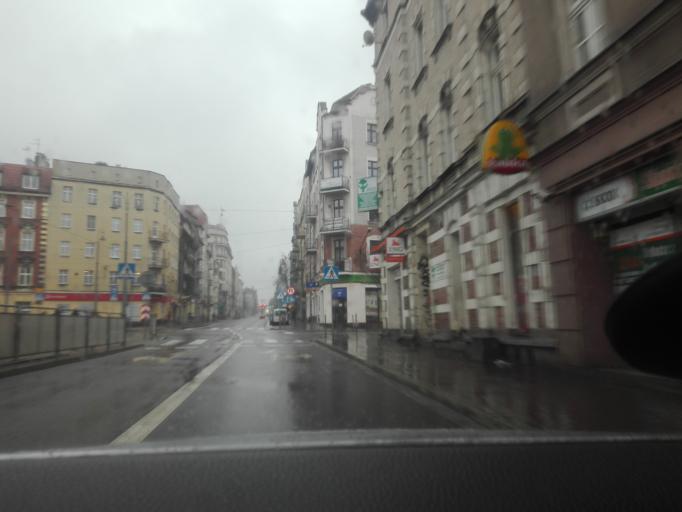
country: PL
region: Silesian Voivodeship
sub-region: Katowice
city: Katowice
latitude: 50.2547
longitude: 19.0177
